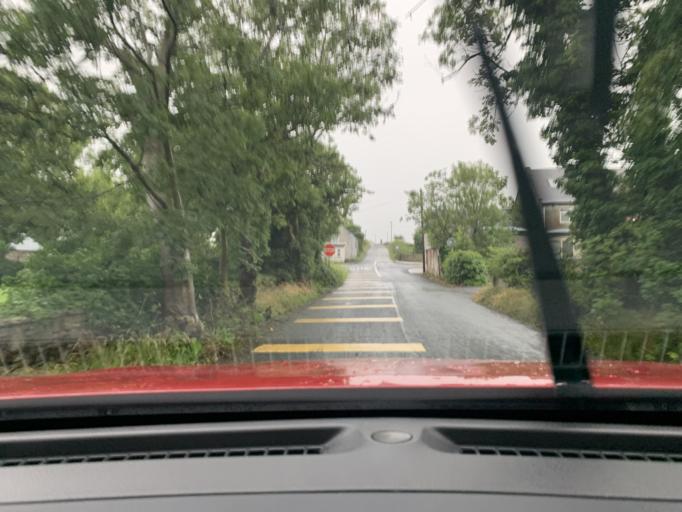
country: IE
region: Connaught
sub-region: County Leitrim
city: Kinlough
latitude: 54.4392
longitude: -8.4357
